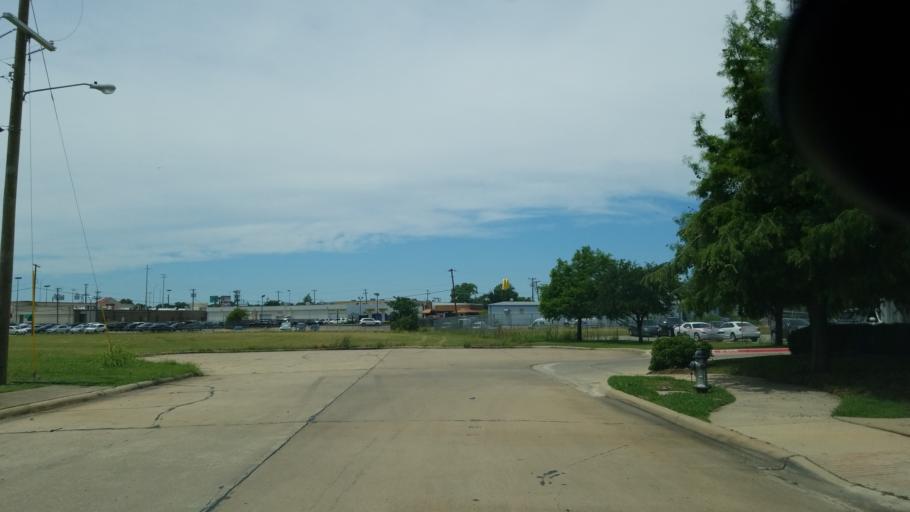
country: US
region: Texas
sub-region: Dallas County
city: Irving
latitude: 32.8405
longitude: -96.9739
